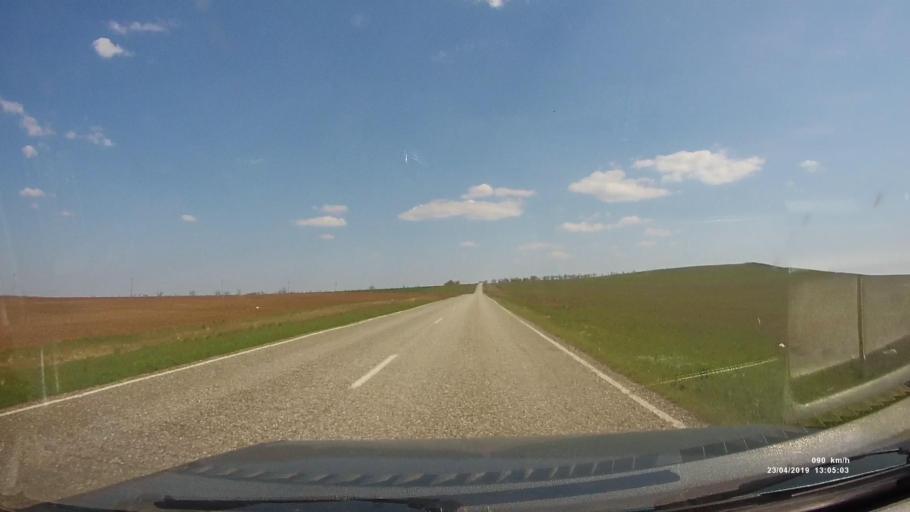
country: RU
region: Kalmykiya
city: Yashalta
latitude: 46.5928
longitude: 42.7156
